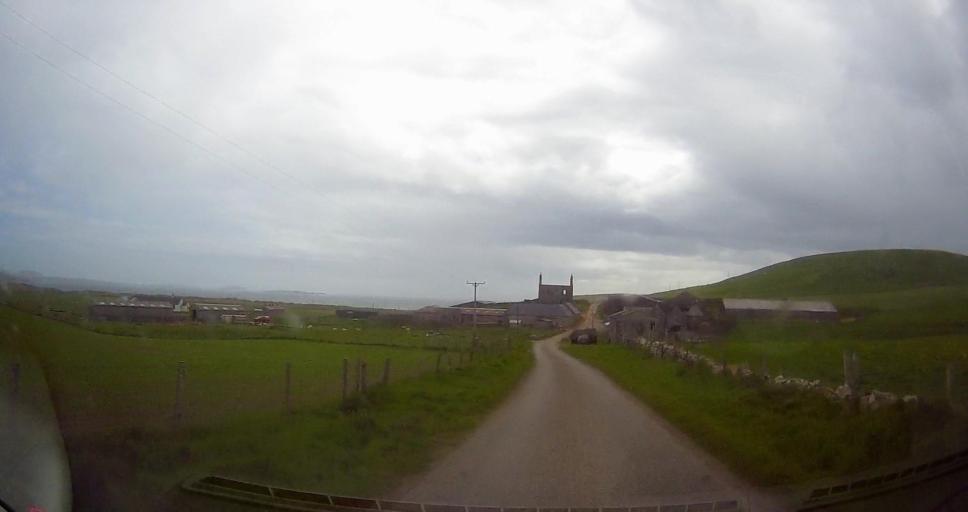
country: GB
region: Scotland
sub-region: Shetland Islands
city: Sandwick
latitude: 59.9040
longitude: -1.3367
